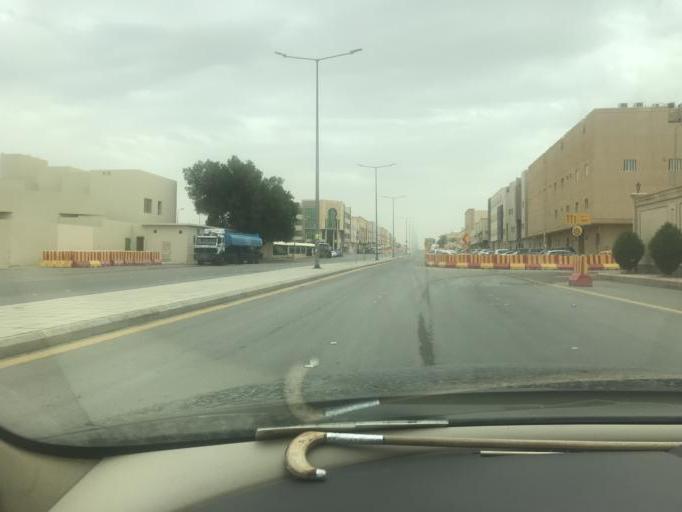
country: SA
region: Ar Riyad
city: Riyadh
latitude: 24.7967
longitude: 46.7080
